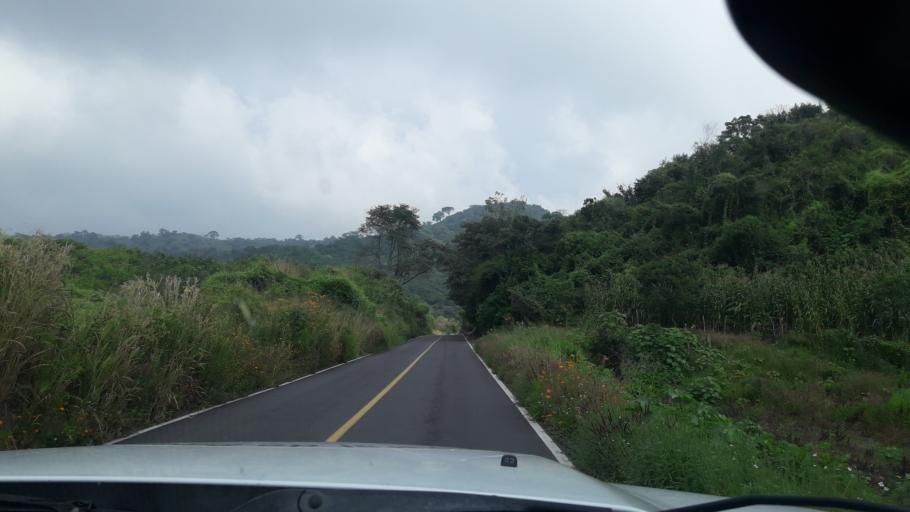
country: MX
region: Colima
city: Suchitlan
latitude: 19.4127
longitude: -103.6511
